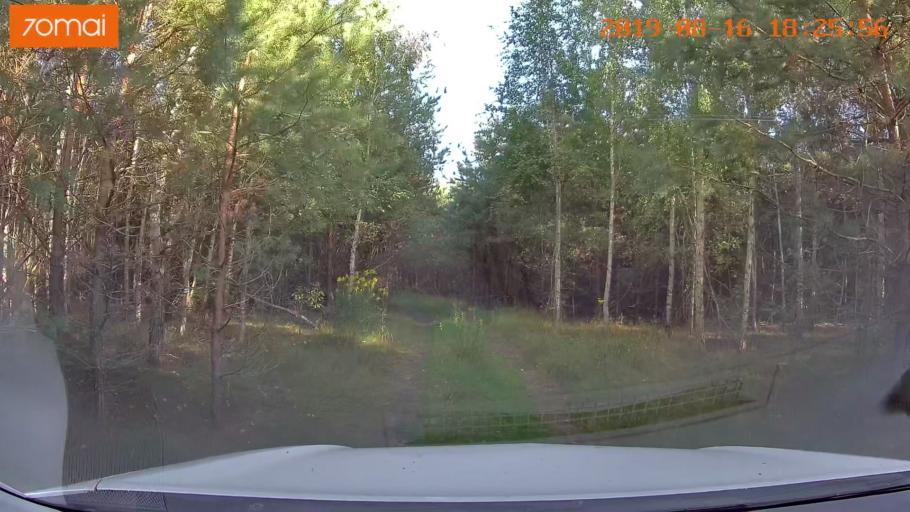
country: BY
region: Mogilev
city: Asipovichy
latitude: 53.2034
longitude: 28.6382
